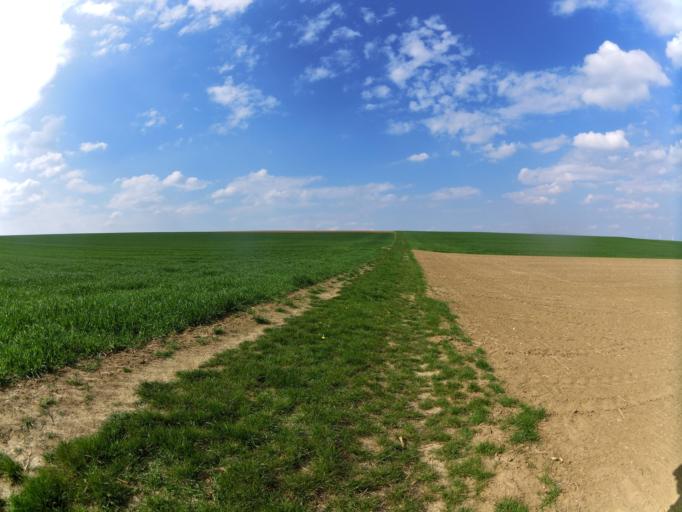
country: DE
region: Bavaria
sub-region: Regierungsbezirk Unterfranken
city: Winterhausen
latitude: 49.6872
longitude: 10.0058
